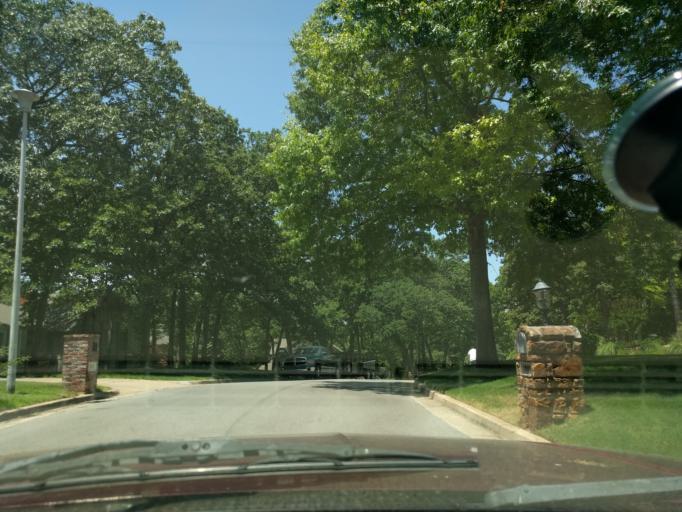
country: US
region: Oklahoma
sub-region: Tulsa County
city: Jenks
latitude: 36.0201
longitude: -95.9327
